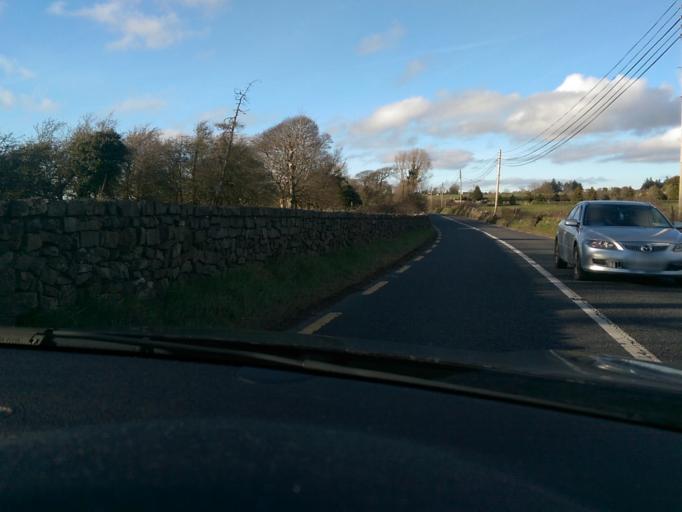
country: IE
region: Connaught
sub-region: Roscommon
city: Roscommon
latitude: 53.6570
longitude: -8.1984
